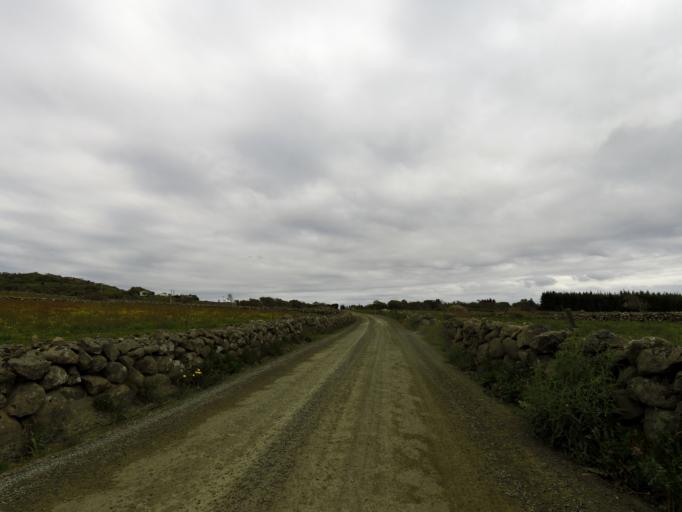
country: NO
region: Vest-Agder
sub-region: Farsund
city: Vestbygd
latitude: 58.1327
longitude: 6.6090
